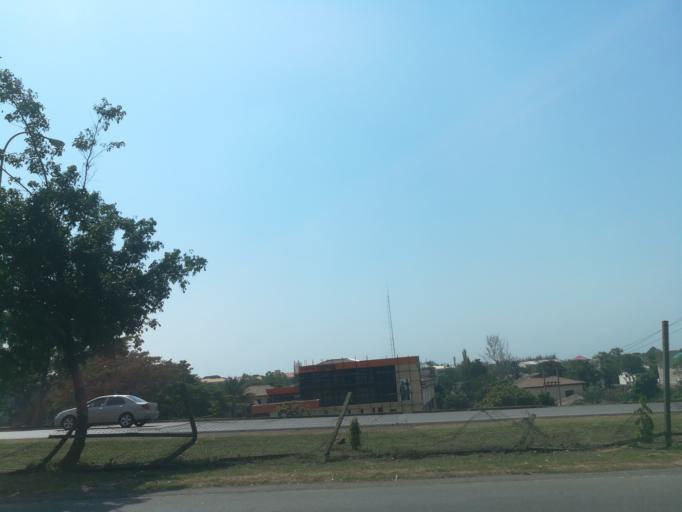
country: NG
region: Abuja Federal Capital Territory
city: Abuja
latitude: 9.0789
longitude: 7.4522
